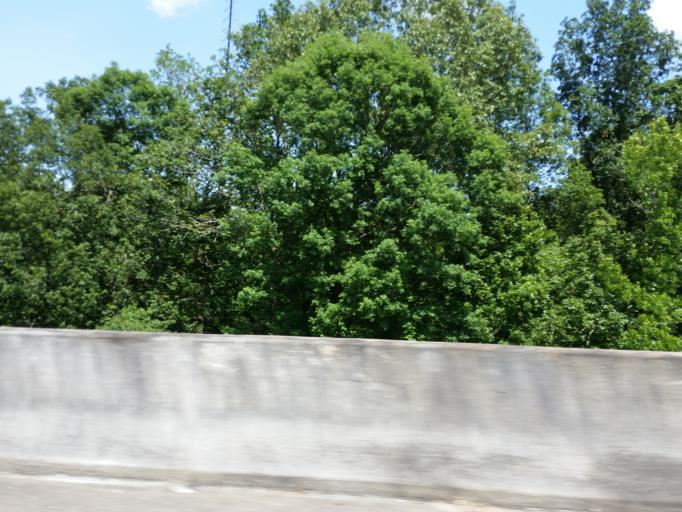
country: US
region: Alabama
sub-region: Marengo County
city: Demopolis
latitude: 32.5489
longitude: -87.8350
